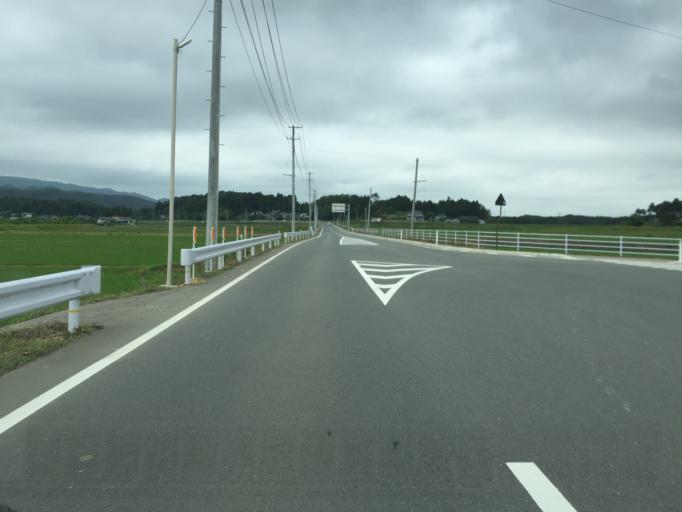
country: JP
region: Miyagi
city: Marumori
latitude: 37.7336
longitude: 140.9275
